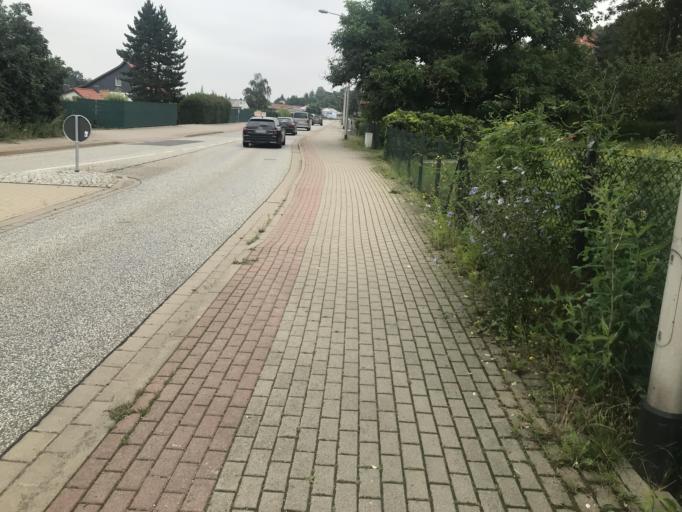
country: DE
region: Saxony-Anhalt
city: Quedlinburg
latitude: 51.7935
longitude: 11.1221
